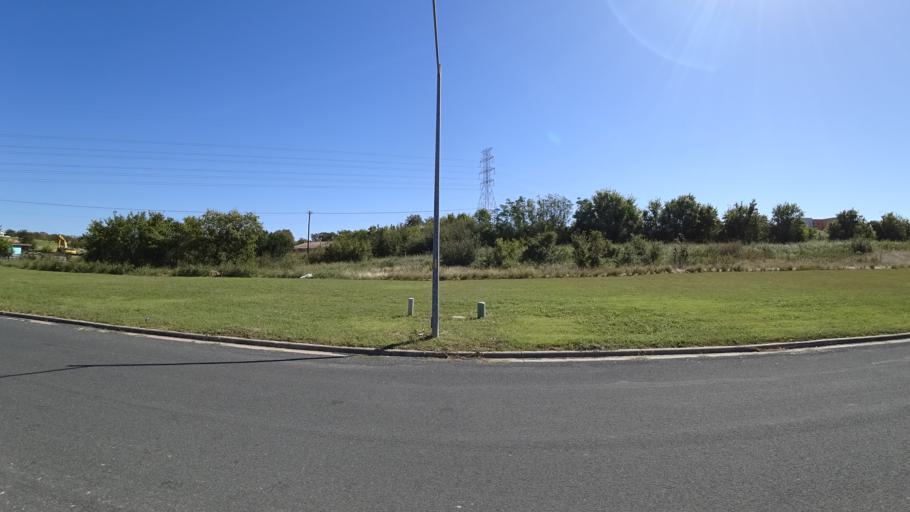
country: US
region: Texas
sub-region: Travis County
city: Hornsby Bend
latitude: 30.2877
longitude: -97.6443
